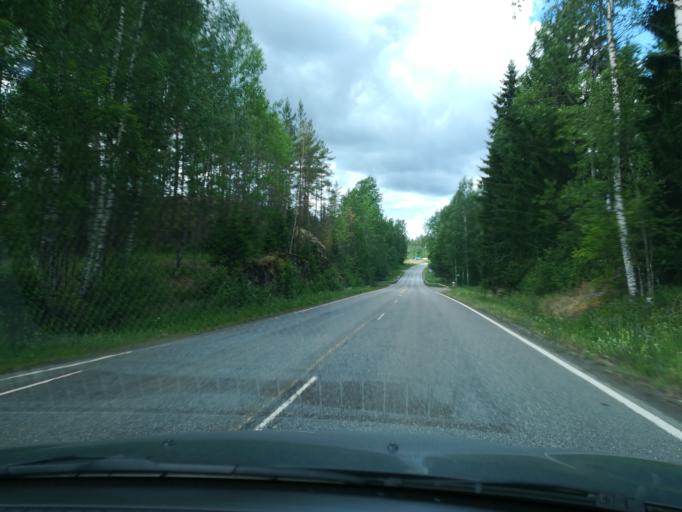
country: FI
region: Southern Savonia
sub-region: Mikkeli
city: Maentyharju
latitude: 61.3666
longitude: 26.9326
